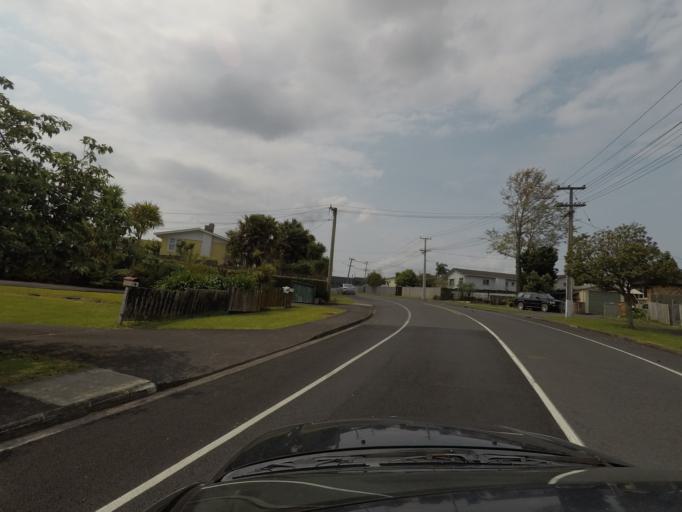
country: NZ
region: Auckland
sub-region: Auckland
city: Rosebank
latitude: -36.8327
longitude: 174.6457
